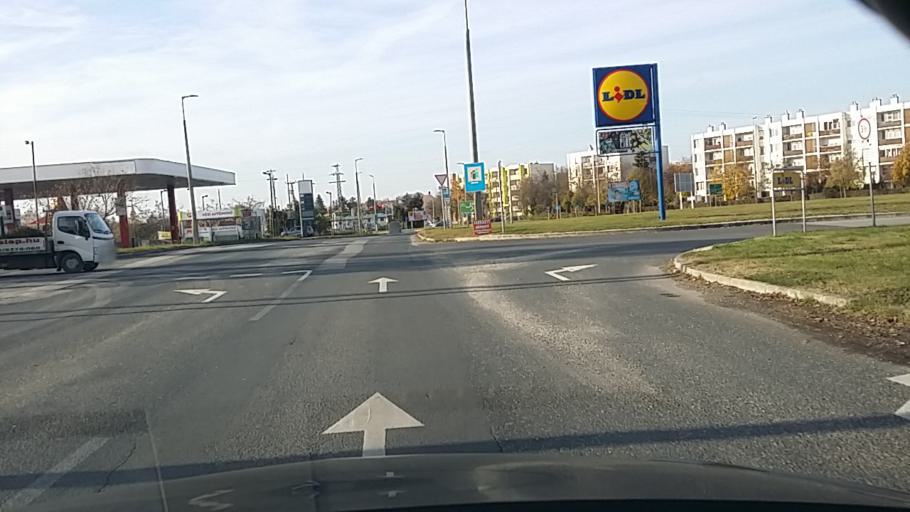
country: HU
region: Veszprem
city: Tapolca
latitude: 46.8796
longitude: 17.4524
